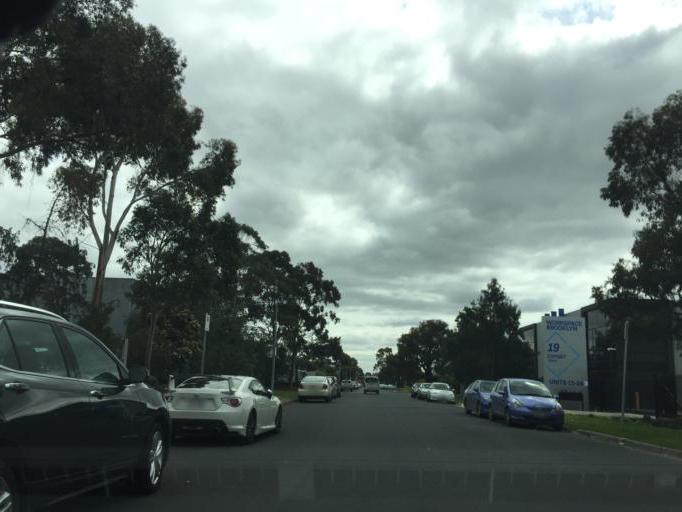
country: AU
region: Victoria
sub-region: Brimbank
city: Brooklyn
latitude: -37.8209
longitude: 144.8550
